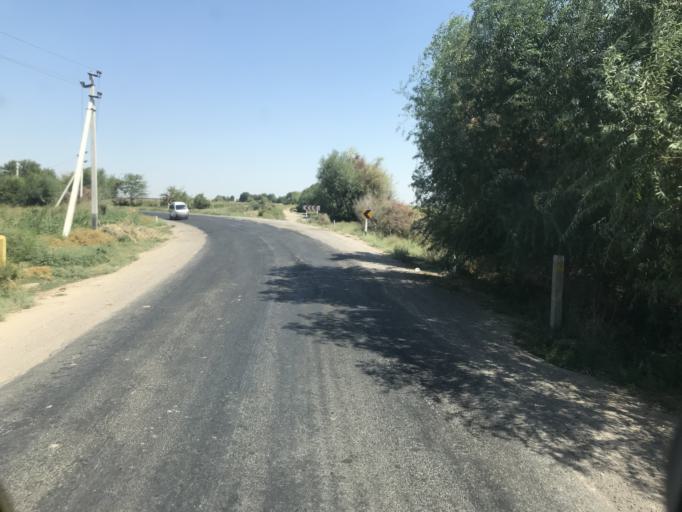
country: KZ
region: Ongtustik Qazaqstan
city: Ilyich
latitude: 40.9472
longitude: 68.4890
